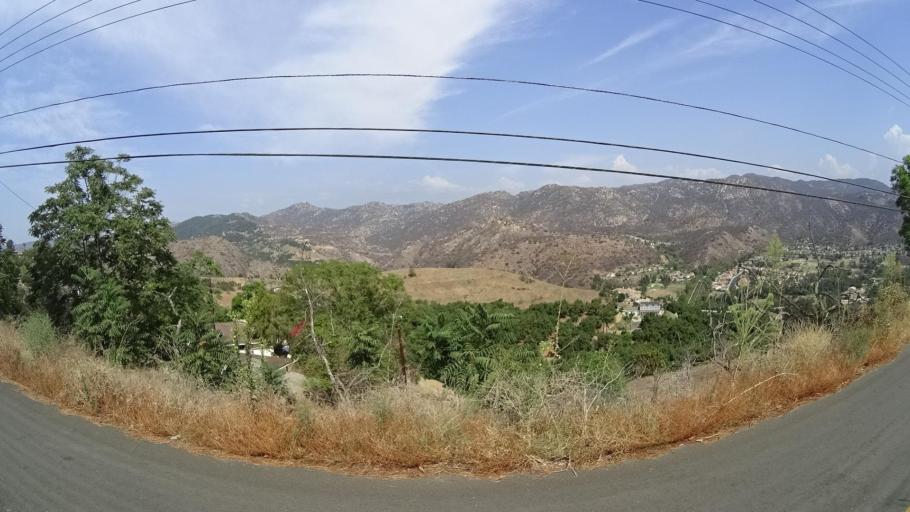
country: US
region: California
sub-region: San Diego County
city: Escondido
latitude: 33.1215
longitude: -117.0216
